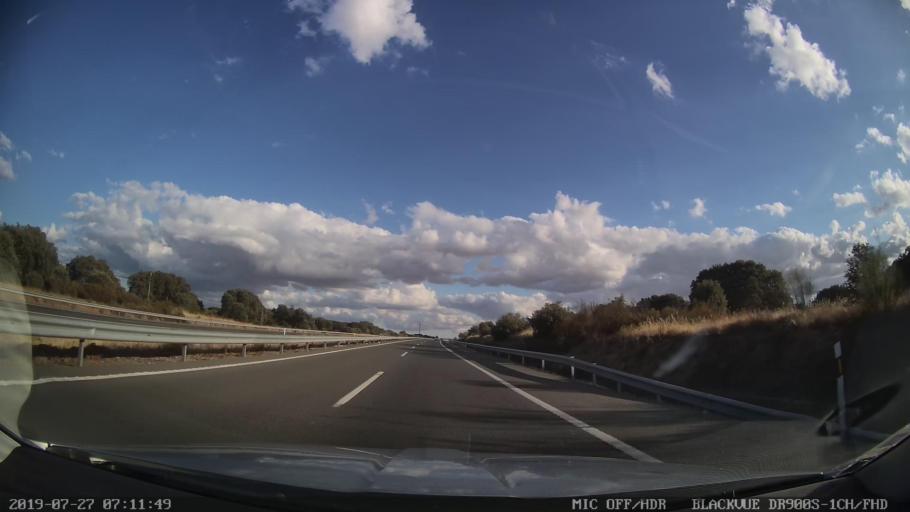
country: ES
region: Extremadura
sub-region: Provincia de Caceres
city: Torrecillas de la Tiesa
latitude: 39.5450
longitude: -5.8335
